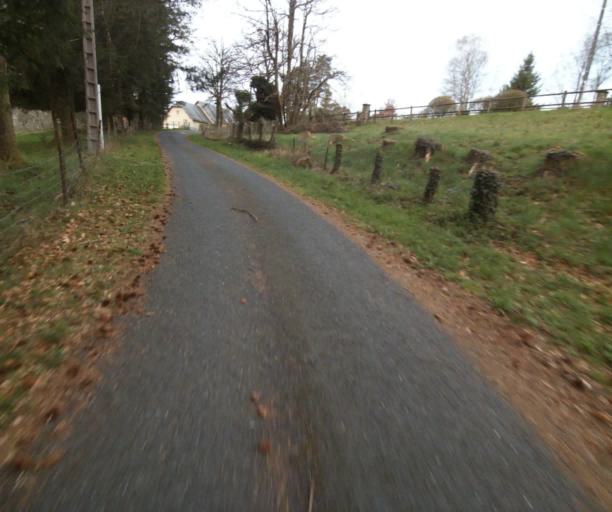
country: FR
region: Limousin
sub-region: Departement de la Correze
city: Correze
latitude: 45.4248
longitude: 1.8439
